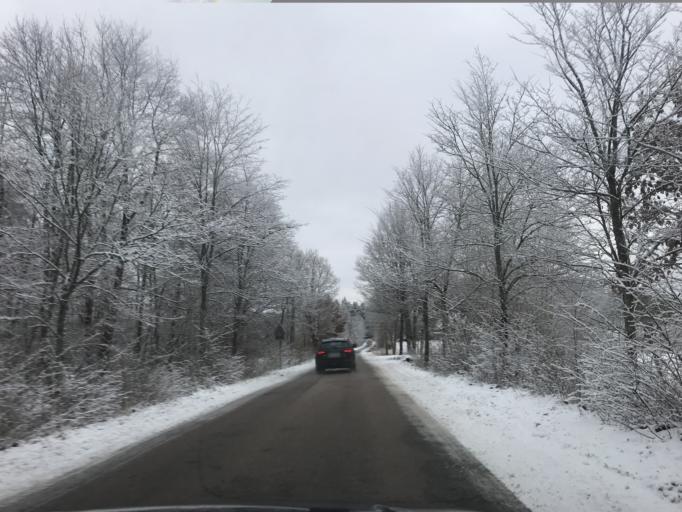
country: PL
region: Pomeranian Voivodeship
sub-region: Powiat bytowski
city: Parchowo
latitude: 54.2381
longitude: 17.5760
